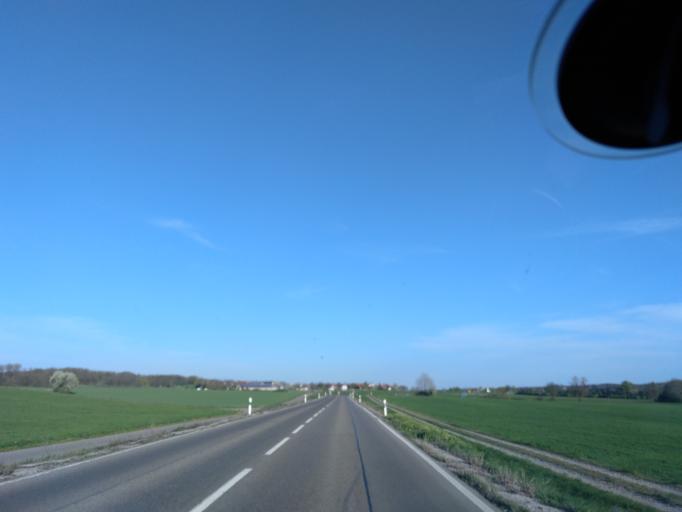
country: DE
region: Baden-Wuerttemberg
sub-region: Regierungsbezirk Stuttgart
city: Kirchberg an der Jagst
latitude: 49.1582
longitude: 9.9640
